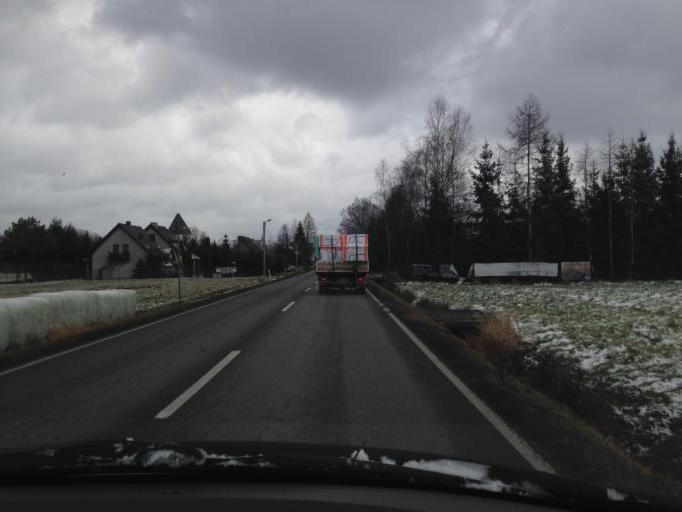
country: PL
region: Lesser Poland Voivodeship
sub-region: Powiat bochenski
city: Lapanow
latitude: 49.8597
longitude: 20.3332
